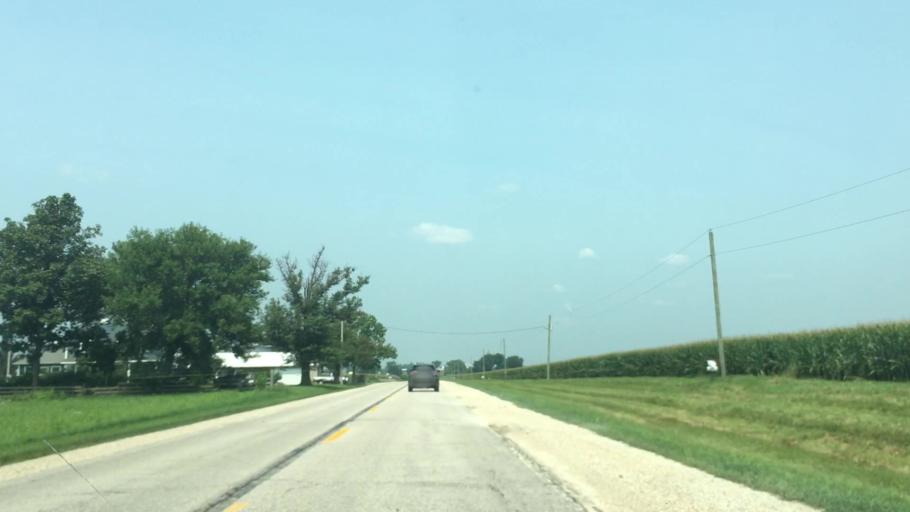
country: US
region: Iowa
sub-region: Benton County
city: Urbana
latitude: 42.3033
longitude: -91.8894
